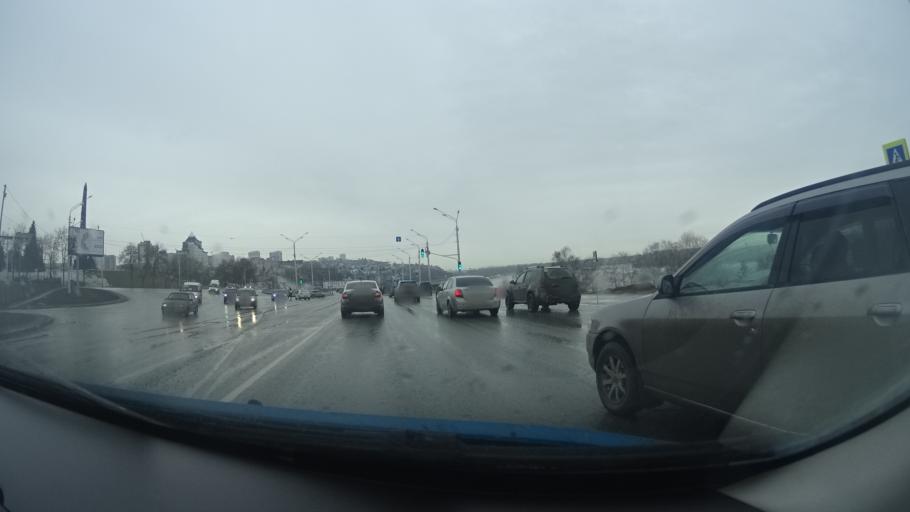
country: RU
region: Bashkortostan
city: Ufa
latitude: 54.7121
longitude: 55.9609
